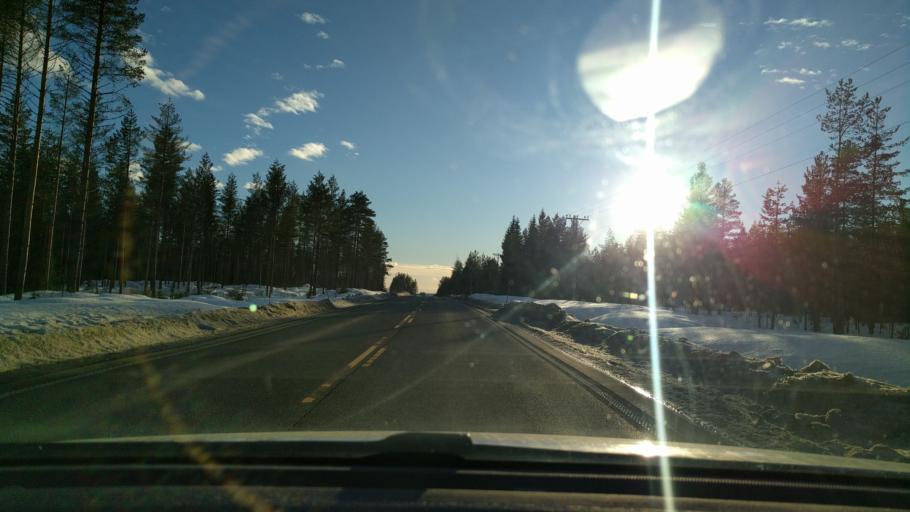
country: NO
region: Hedmark
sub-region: Elverum
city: Elverum
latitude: 61.0163
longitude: 11.8450
